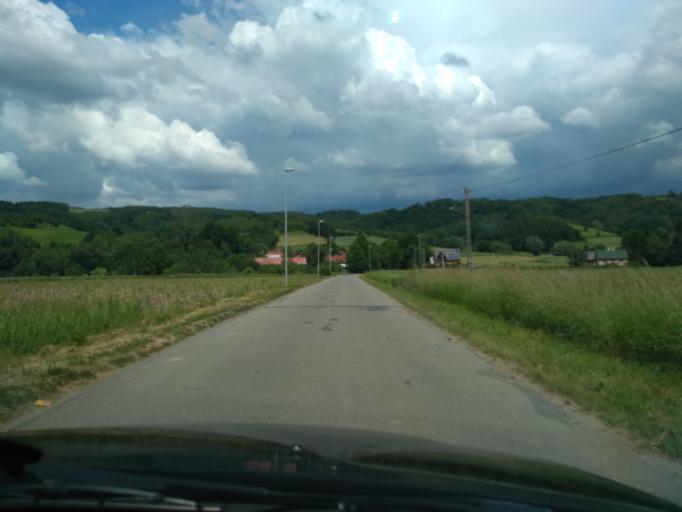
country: PL
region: Subcarpathian Voivodeship
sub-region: Powiat strzyzowski
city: Strzyzow
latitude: 49.8358
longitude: 21.8310
